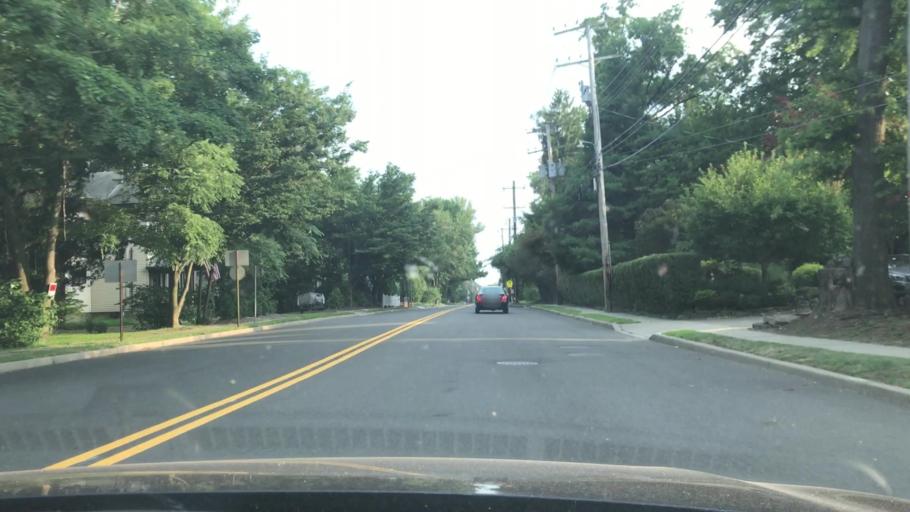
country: US
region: New Jersey
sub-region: Bergen County
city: Norwood
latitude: 40.9958
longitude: -73.9563
